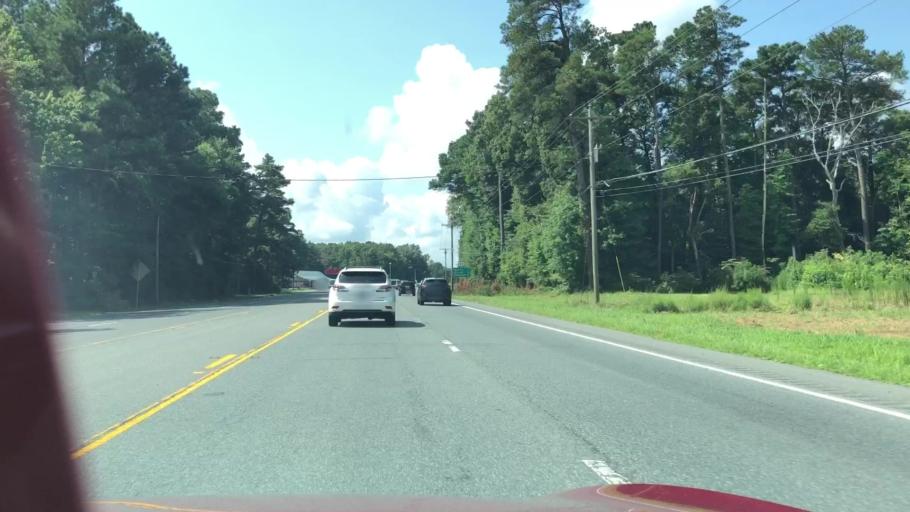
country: US
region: Virginia
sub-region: Accomack County
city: Wattsville
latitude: 37.8407
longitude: -75.5706
